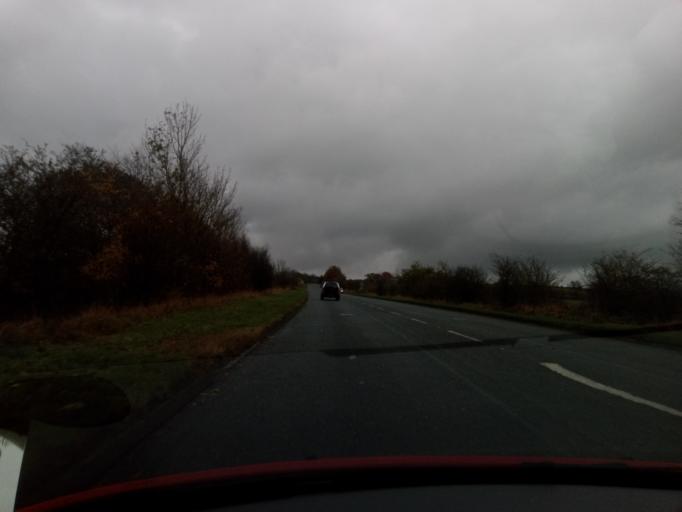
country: GB
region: England
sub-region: County Durham
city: High Etherley
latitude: 54.6604
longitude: -1.7720
